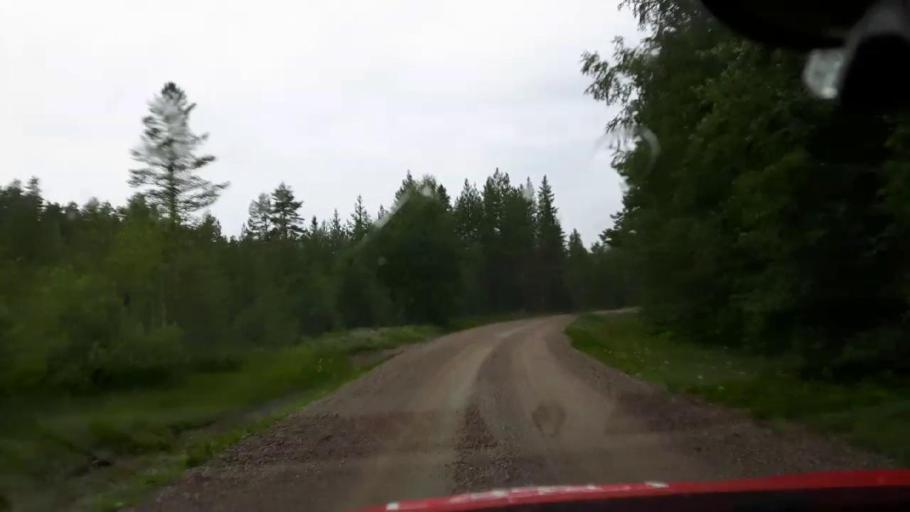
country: SE
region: Jaemtland
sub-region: OEstersunds Kommun
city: Brunflo
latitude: 62.8101
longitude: 14.8886
